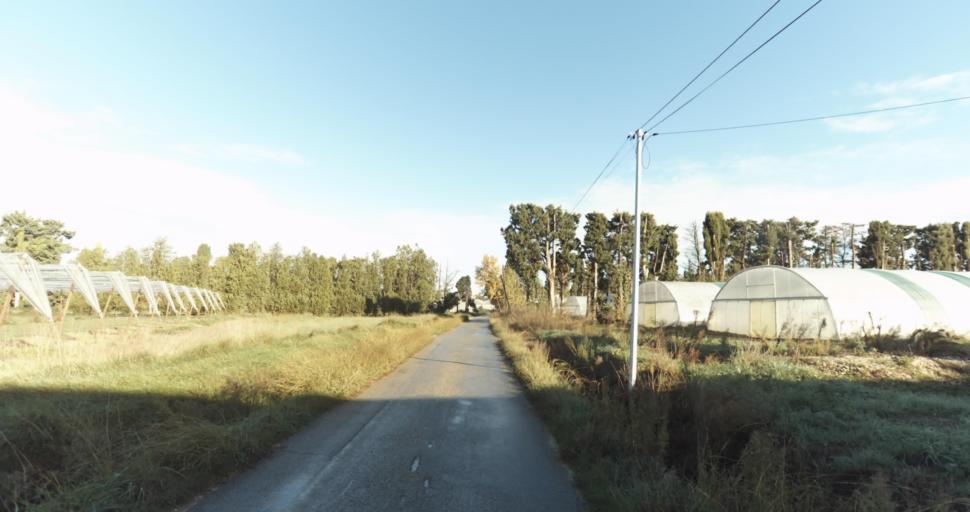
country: FR
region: Provence-Alpes-Cote d'Azur
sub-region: Departement des Bouches-du-Rhone
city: Rognonas
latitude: 43.8865
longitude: 4.7926
